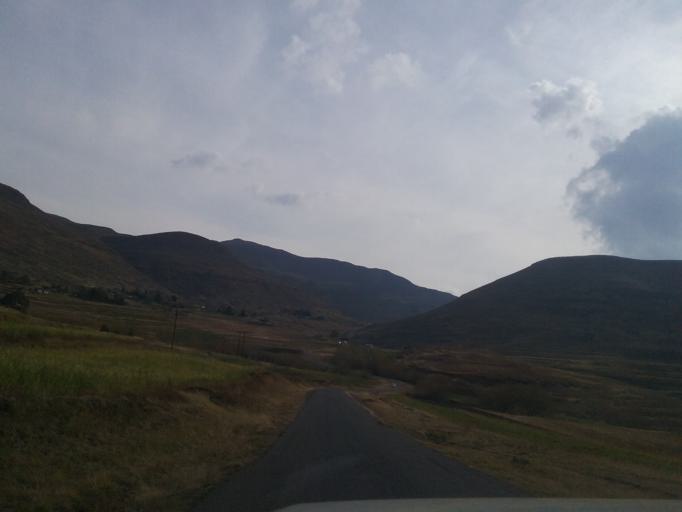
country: LS
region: Quthing
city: Quthing
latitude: -30.1898
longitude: 28.0868
